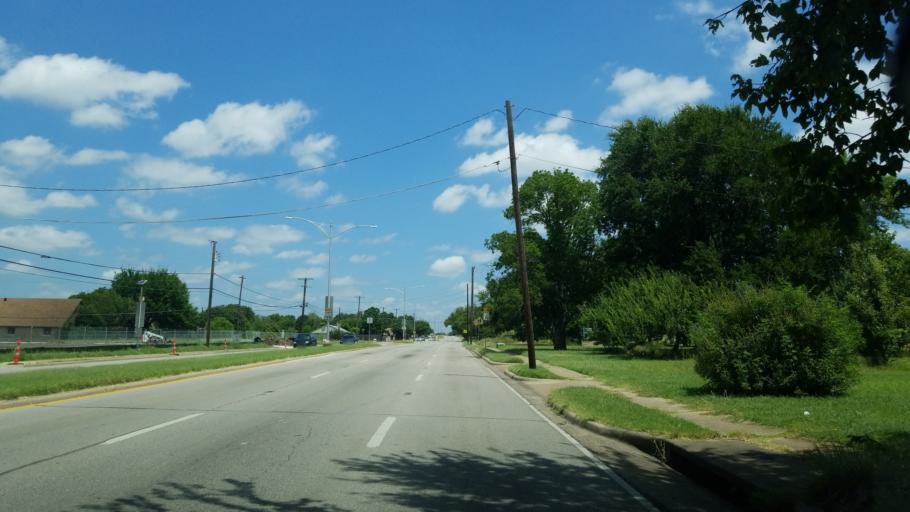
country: US
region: Texas
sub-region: Dallas County
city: Balch Springs
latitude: 32.7396
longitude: -96.7001
